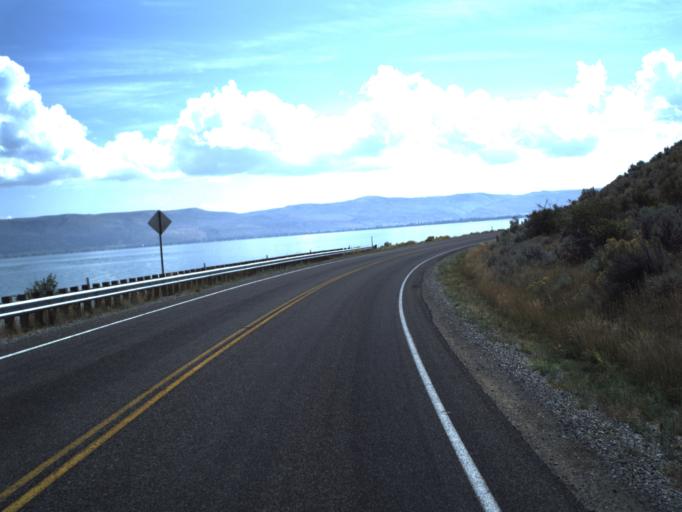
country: US
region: Utah
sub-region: Rich County
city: Randolph
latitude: 41.8977
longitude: -111.3673
